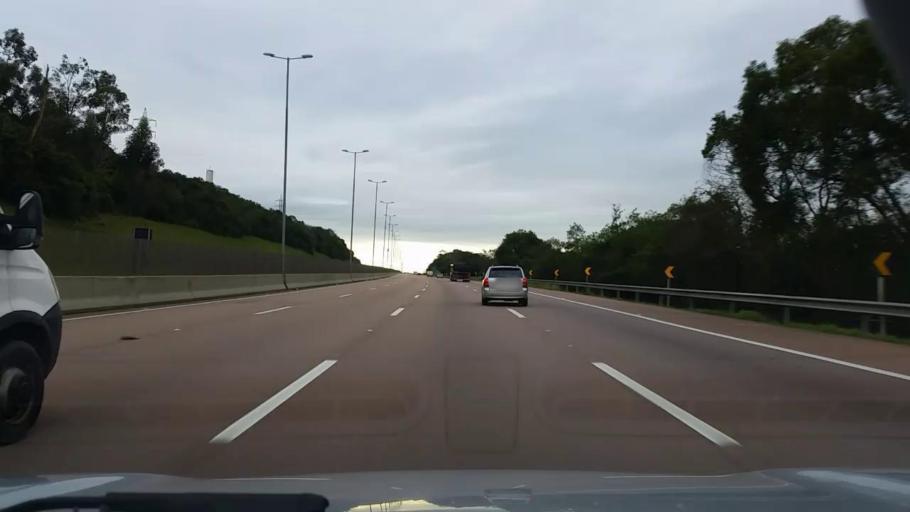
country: BR
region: Rio Grande do Sul
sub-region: Gravatai
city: Gravatai
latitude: -29.9566
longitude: -51.0131
